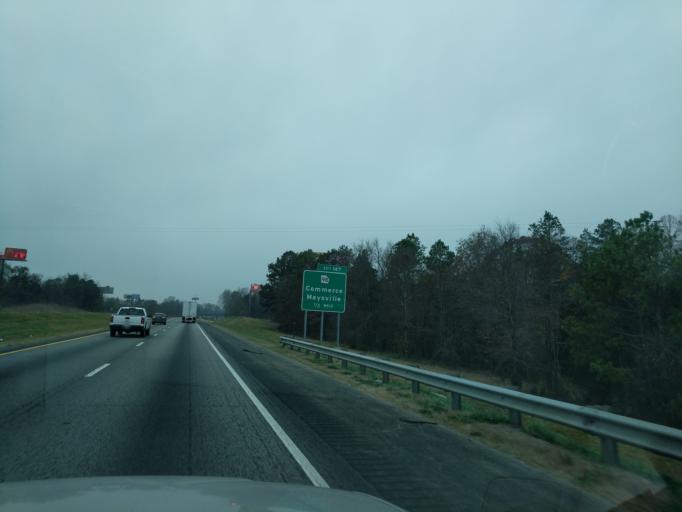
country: US
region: Georgia
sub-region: Jackson County
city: Commerce
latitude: 34.2355
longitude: -83.4916
